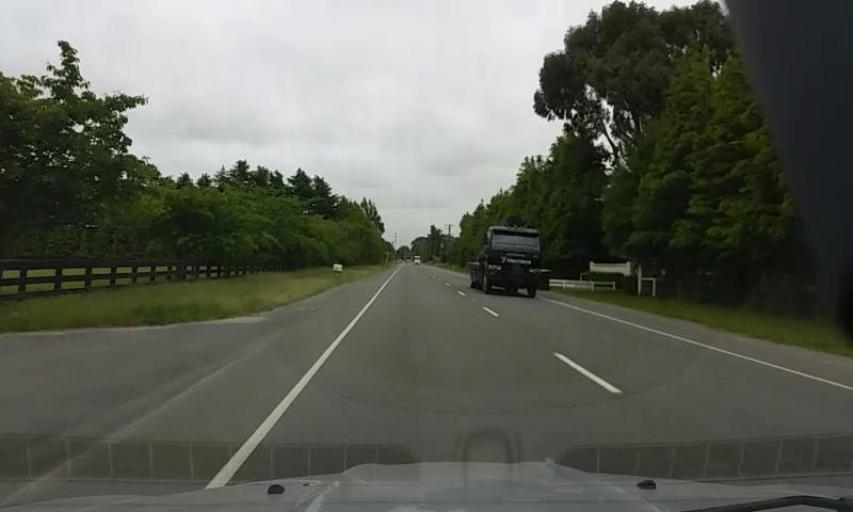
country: NZ
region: Canterbury
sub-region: Selwyn District
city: Prebbleton
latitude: -43.5146
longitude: 172.5155
